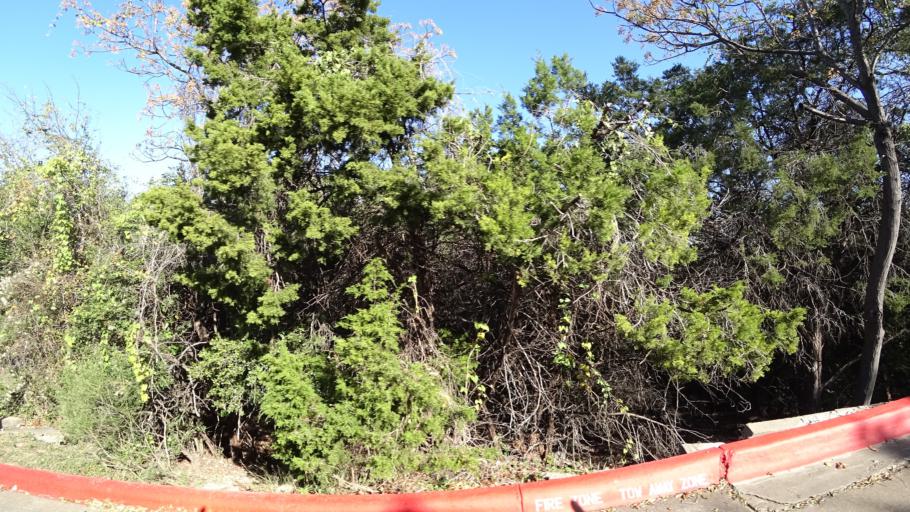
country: US
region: Texas
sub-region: Williamson County
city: Jollyville
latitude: 30.4026
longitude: -97.7554
